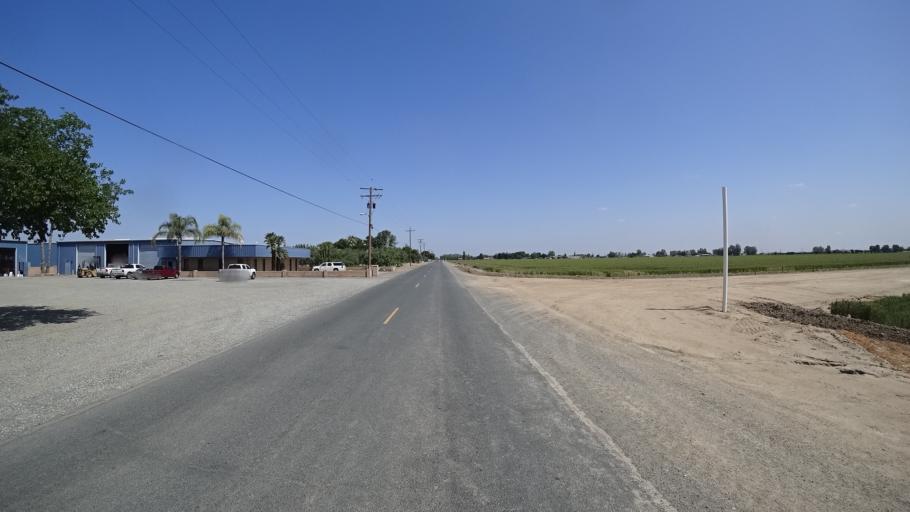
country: US
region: California
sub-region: Kings County
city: Home Garden
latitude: 36.2908
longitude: -119.6190
